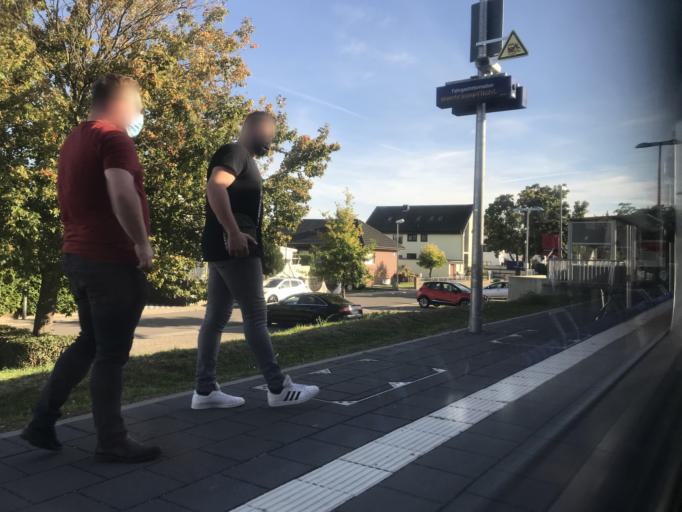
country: DE
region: Rheinland-Pfalz
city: Alsheim
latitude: 49.7655
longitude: 8.3427
